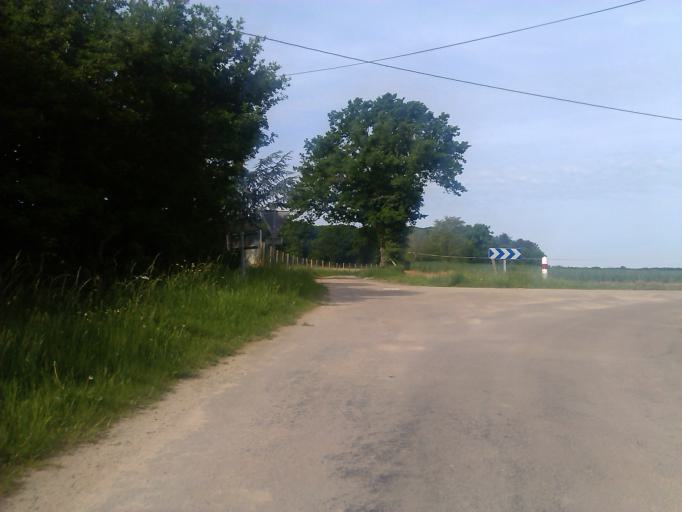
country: FR
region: Auvergne
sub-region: Departement de l'Allier
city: Ainay-le-Chateau
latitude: 46.6067
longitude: 2.7001
